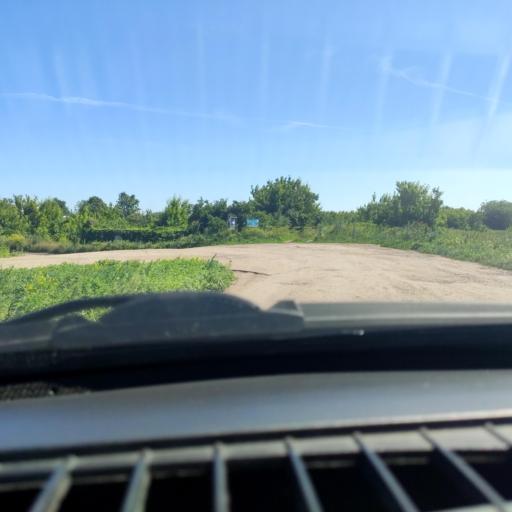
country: RU
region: Samara
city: Tol'yatti
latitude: 53.5913
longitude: 49.4393
